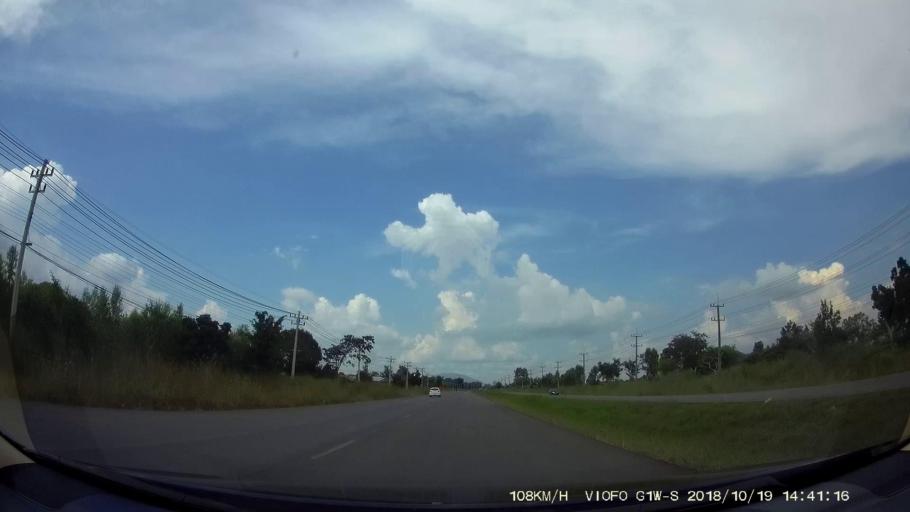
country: TH
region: Chaiyaphum
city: Phu Khiao
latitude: 16.2542
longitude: 102.1986
